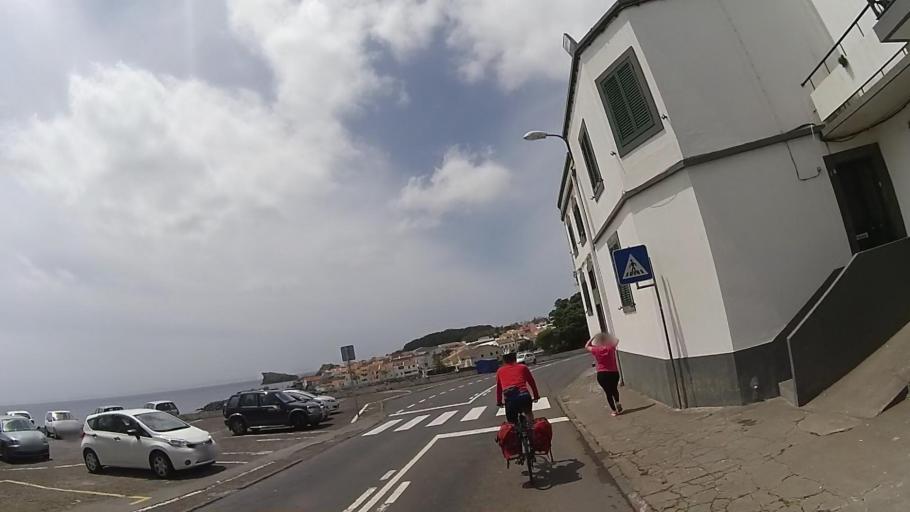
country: PT
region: Azores
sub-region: Ponta Delgada
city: Rosto de Cao
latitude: 37.7506
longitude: -25.6296
